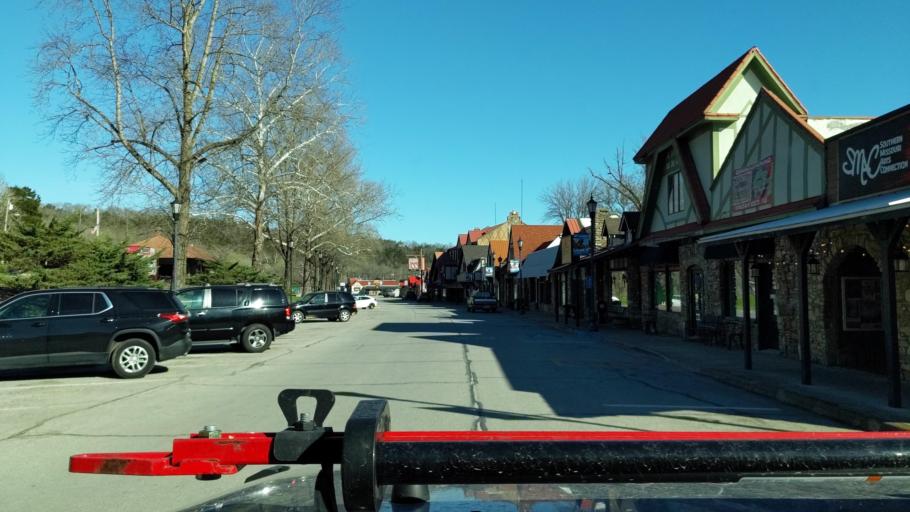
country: US
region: Missouri
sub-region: Taney County
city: Hollister
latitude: 36.6229
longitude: -93.2159
